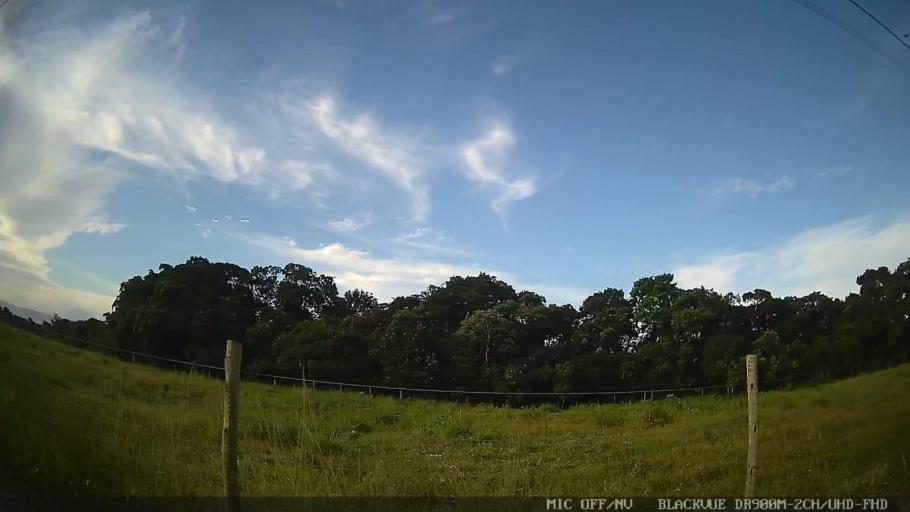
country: BR
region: Sao Paulo
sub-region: Itanhaem
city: Itanhaem
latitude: -24.1535
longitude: -46.7892
